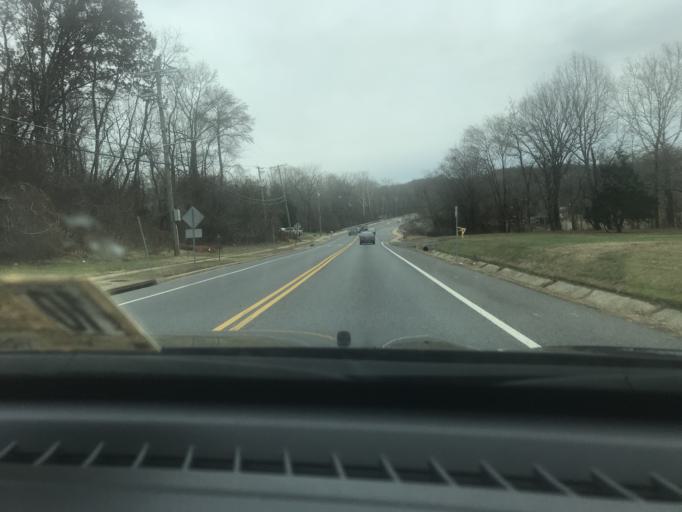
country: US
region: Maryland
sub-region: Prince George's County
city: Temple Hills
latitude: 38.8031
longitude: -76.9491
